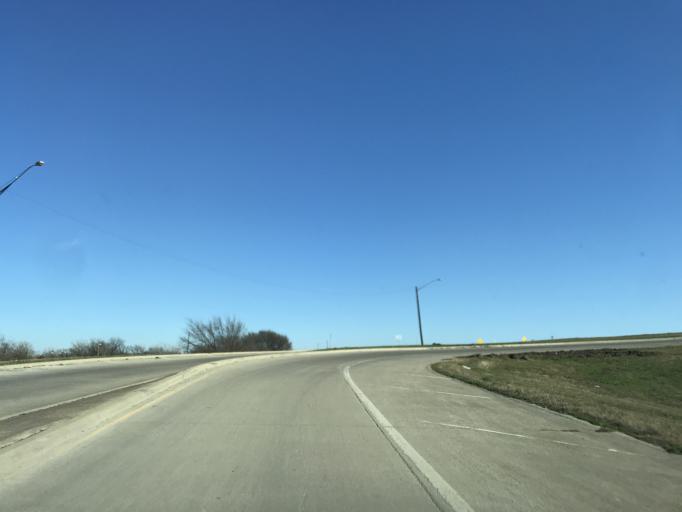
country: US
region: Texas
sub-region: Dallas County
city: Hutchins
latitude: 32.7039
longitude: -96.7471
